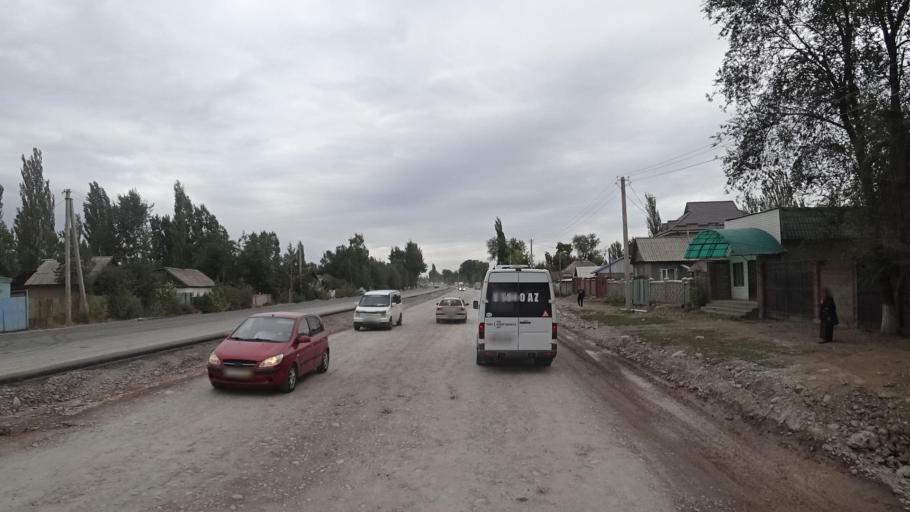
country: KG
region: Chuy
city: Belovodskoye
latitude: 42.8395
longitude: 74.1429
